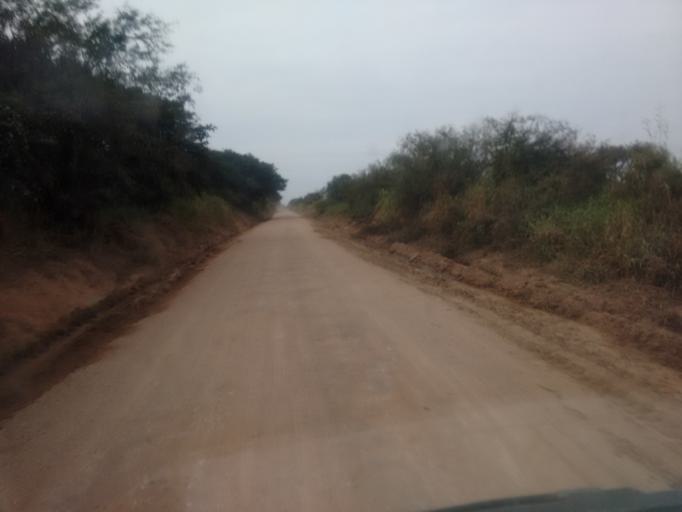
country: BR
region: Rio Grande do Sul
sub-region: Camaqua
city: Camaqua
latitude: -30.9500
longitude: -51.7869
